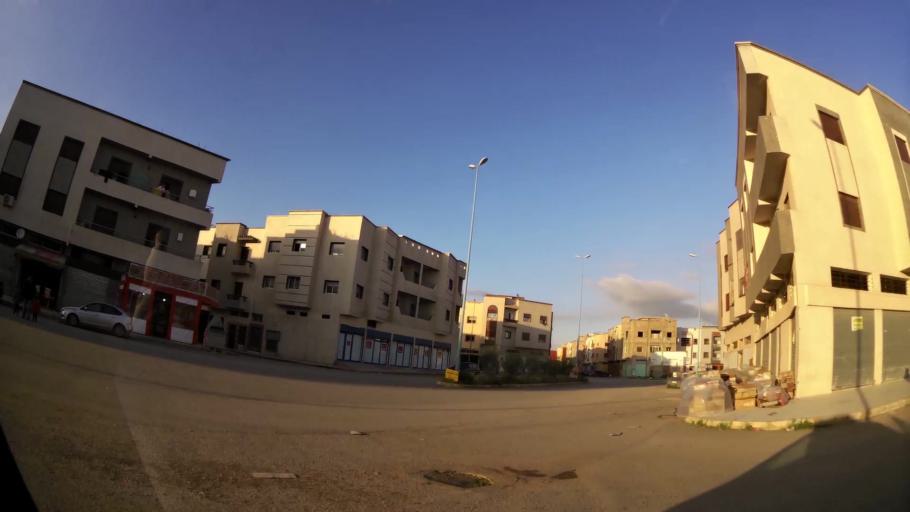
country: MA
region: Chaouia-Ouardigha
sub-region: Settat Province
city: Settat
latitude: 32.9877
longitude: -7.6018
